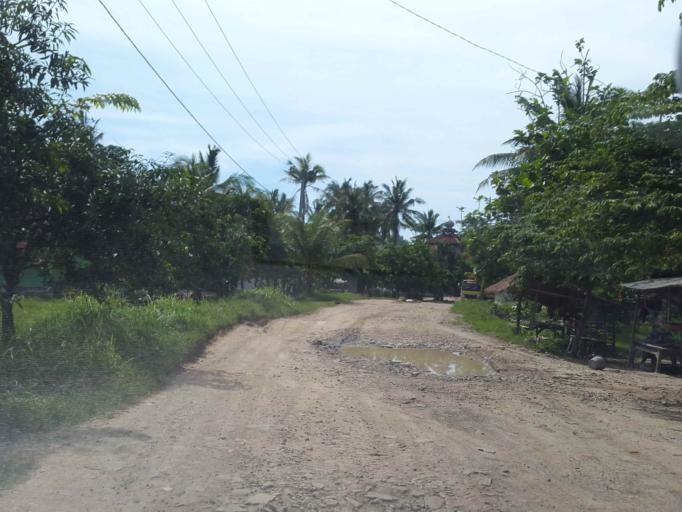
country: ID
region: Banten
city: Citeureup
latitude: -6.4982
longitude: 105.6586
